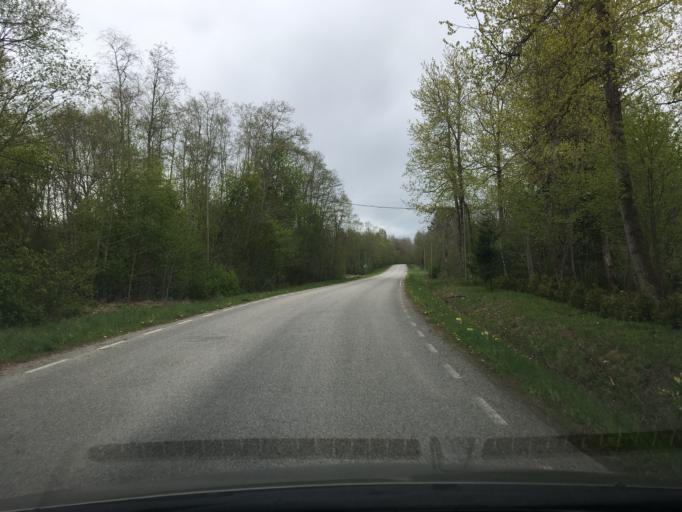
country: EE
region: Harju
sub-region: Rae vald
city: Vaida
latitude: 59.3519
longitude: 24.9954
